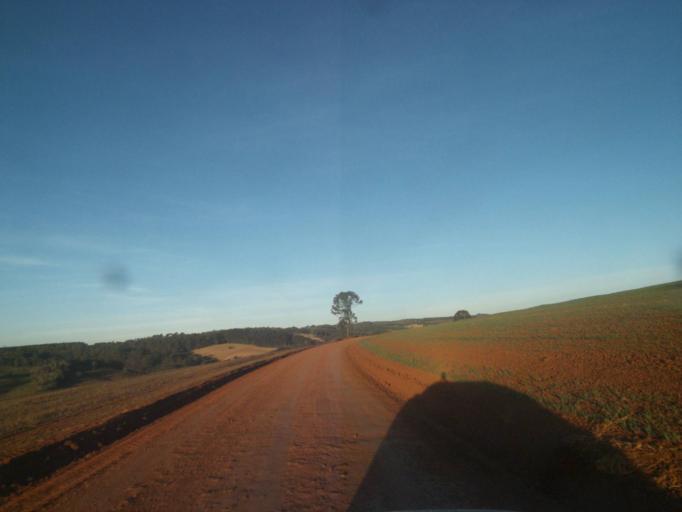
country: BR
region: Parana
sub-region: Tibagi
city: Tibagi
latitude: -24.5229
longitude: -50.4993
